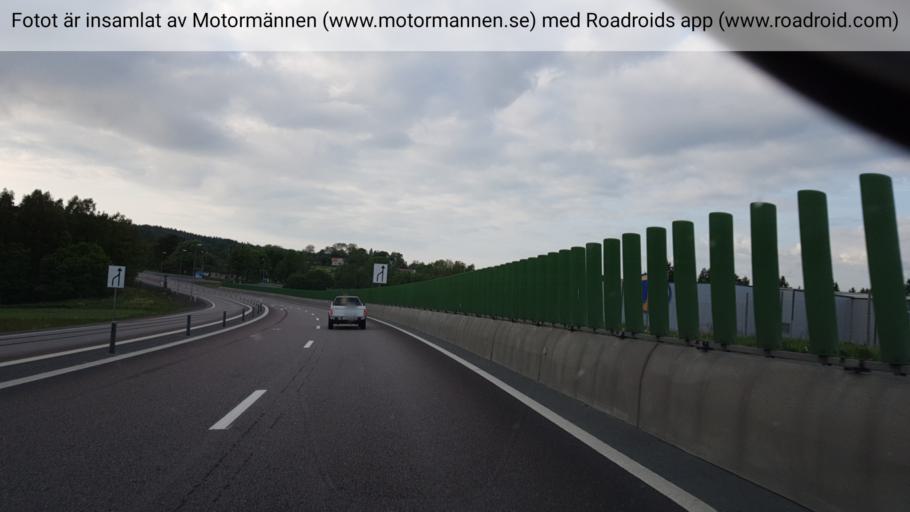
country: SE
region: Joenkoeping
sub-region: Jonkopings Kommun
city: Huskvarna
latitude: 57.7476
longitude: 14.2812
